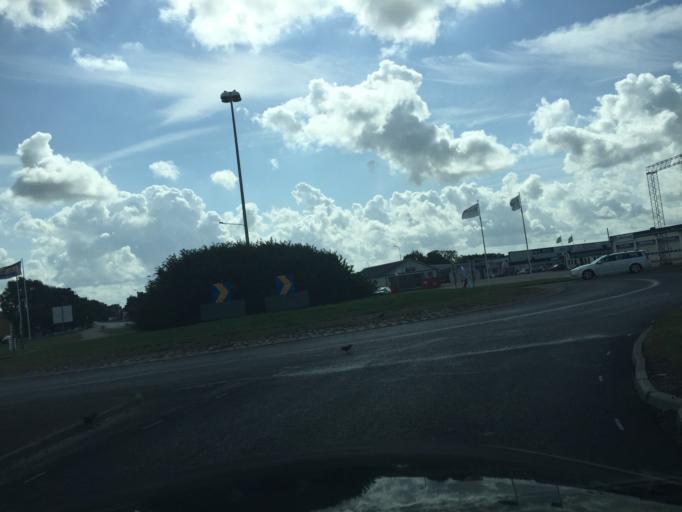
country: SE
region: Halland
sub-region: Laholms Kommun
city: Laholm
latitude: 56.5021
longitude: 13.0333
